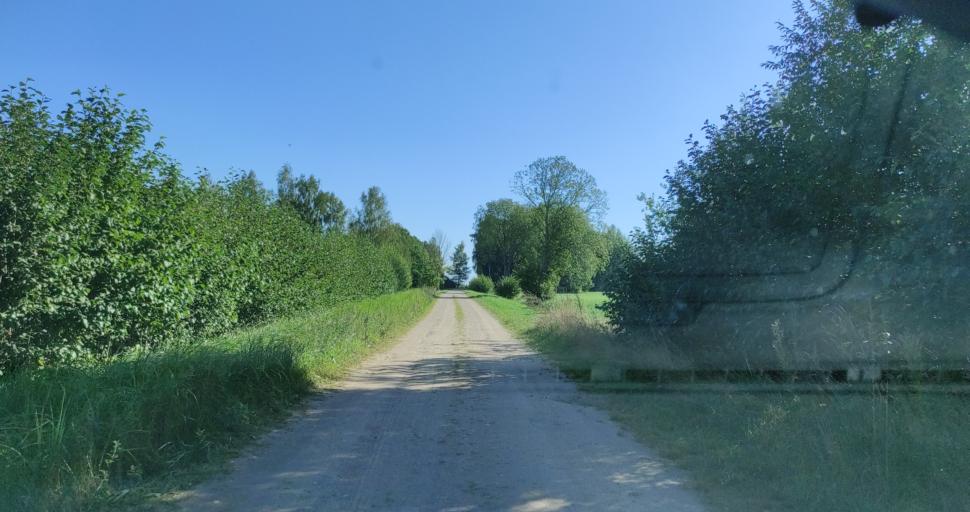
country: LV
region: Kuldigas Rajons
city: Kuldiga
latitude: 56.9735
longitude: 21.9261
